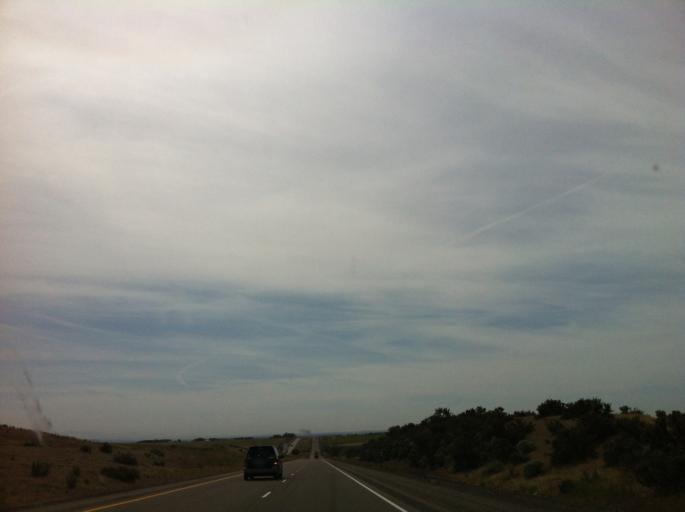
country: US
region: Oregon
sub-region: Malheur County
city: Ontario
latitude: 44.1038
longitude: -117.0454
